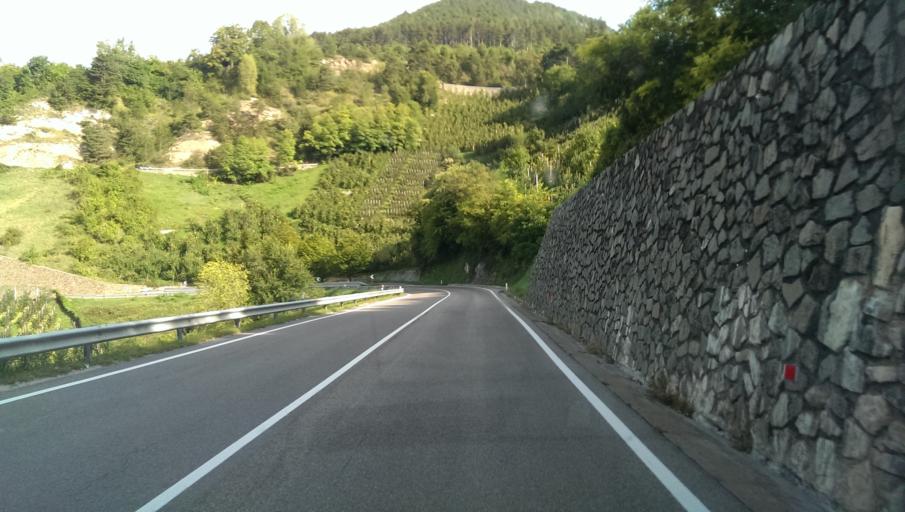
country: IT
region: Trentino-Alto Adige
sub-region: Provincia di Trento
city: Revo
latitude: 46.3921
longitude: 11.0497
